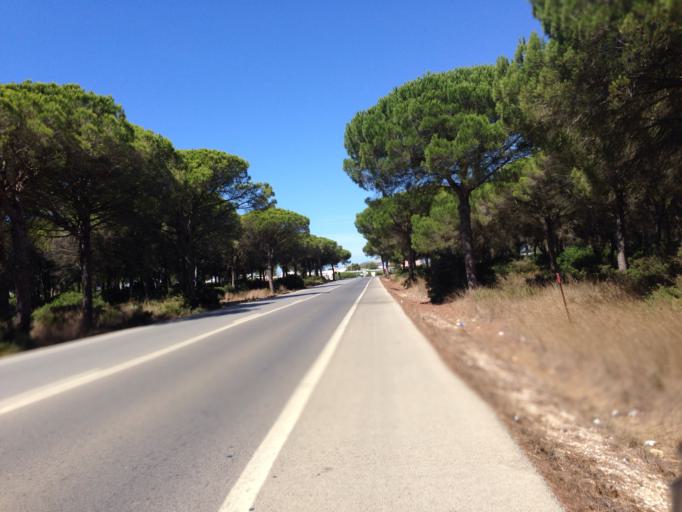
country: ES
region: Andalusia
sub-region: Provincia de Cadiz
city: Conil de la Frontera
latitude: 36.3184
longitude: -6.1057
